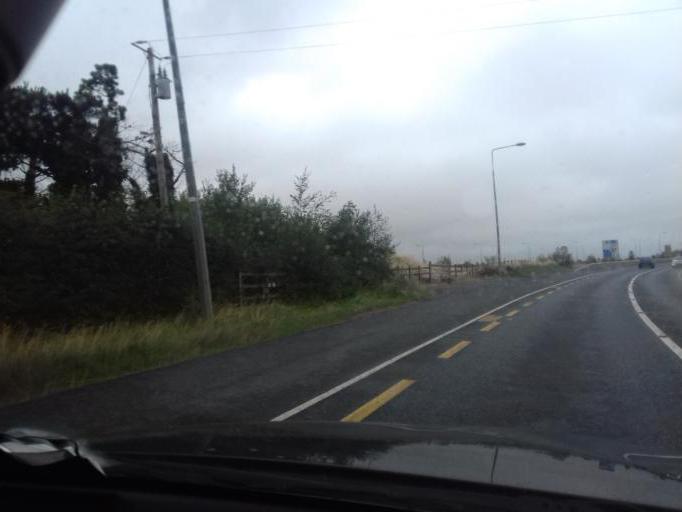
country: IE
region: Leinster
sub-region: County Carlow
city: Bagenalstown
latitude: 52.7672
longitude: -6.9556
